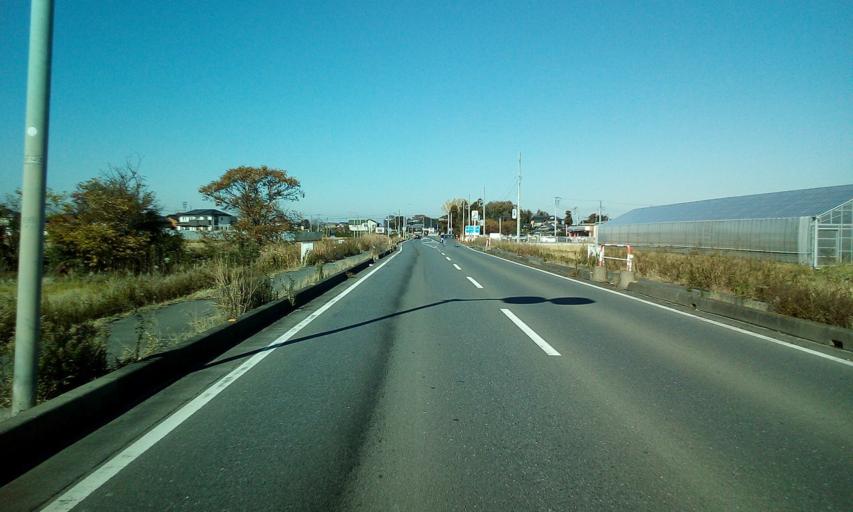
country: JP
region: Chiba
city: Nagareyama
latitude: 35.8860
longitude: 139.8852
